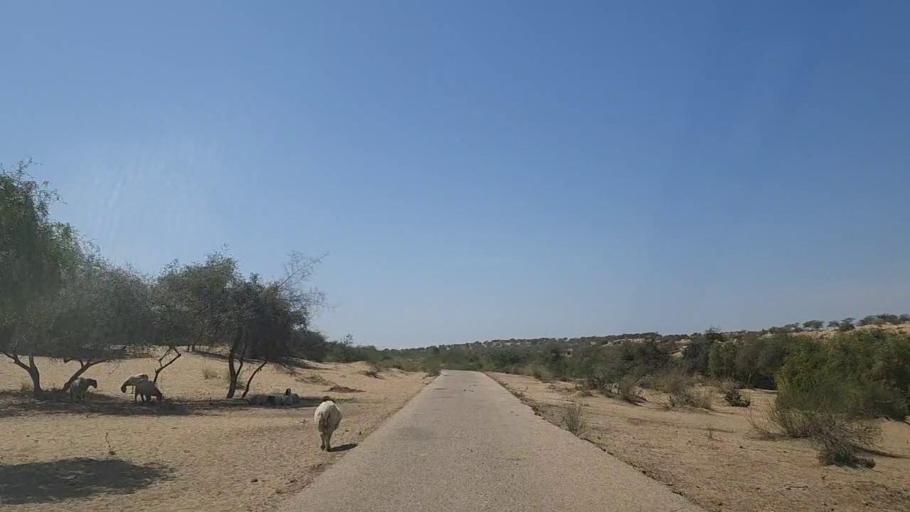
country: PK
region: Sindh
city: Mithi
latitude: 24.8238
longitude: 69.6757
